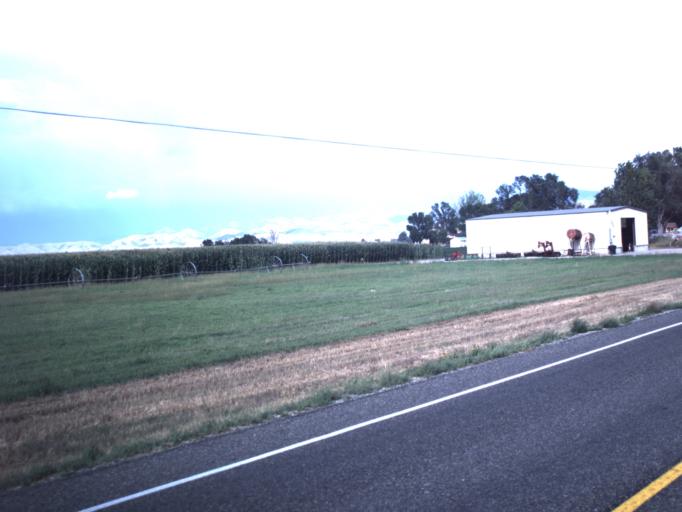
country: US
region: Utah
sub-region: Cache County
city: Lewiston
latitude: 41.9754
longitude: -111.9500
